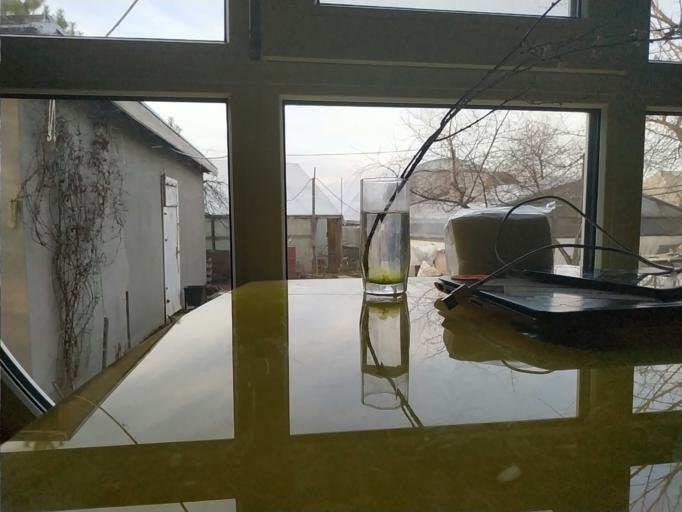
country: RU
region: Republic of Karelia
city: Suoyarvi
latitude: 62.0968
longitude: 32.1654
